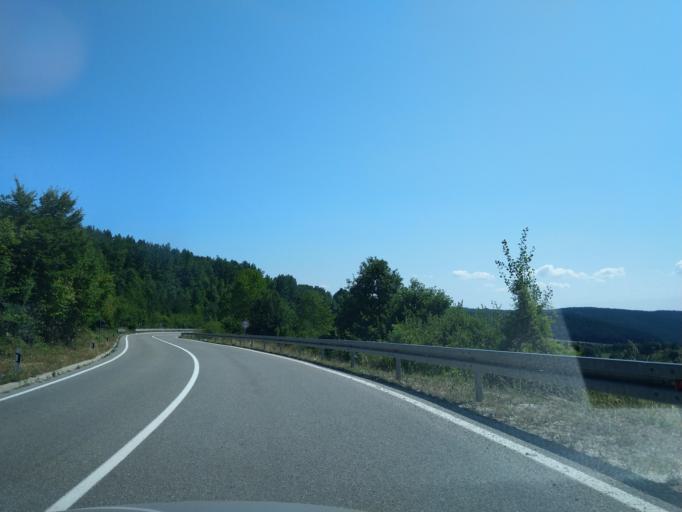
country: RS
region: Central Serbia
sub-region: Zlatiborski Okrug
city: Sjenica
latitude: 43.3067
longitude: 19.9148
